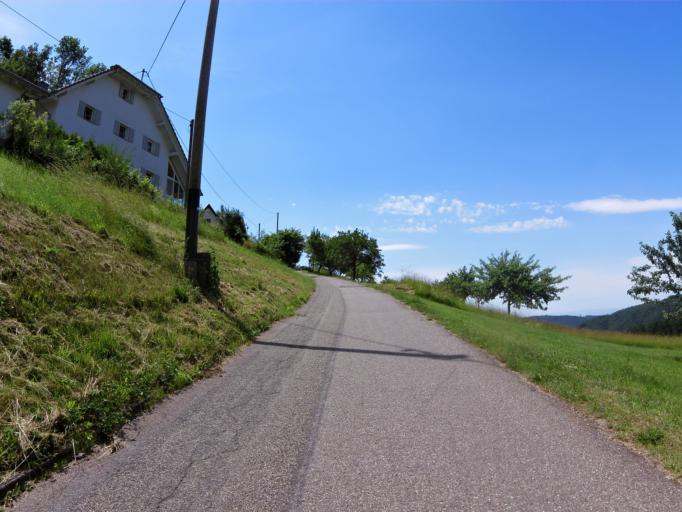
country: DE
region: Baden-Wuerttemberg
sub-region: Freiburg Region
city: Seelbach
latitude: 48.3335
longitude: 7.9787
